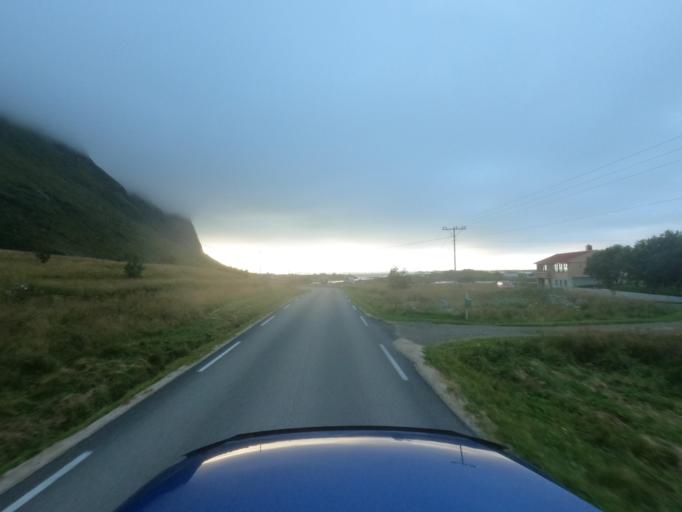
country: NO
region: Nordland
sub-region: Vestvagoy
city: Evjen
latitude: 68.2802
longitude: 13.7221
